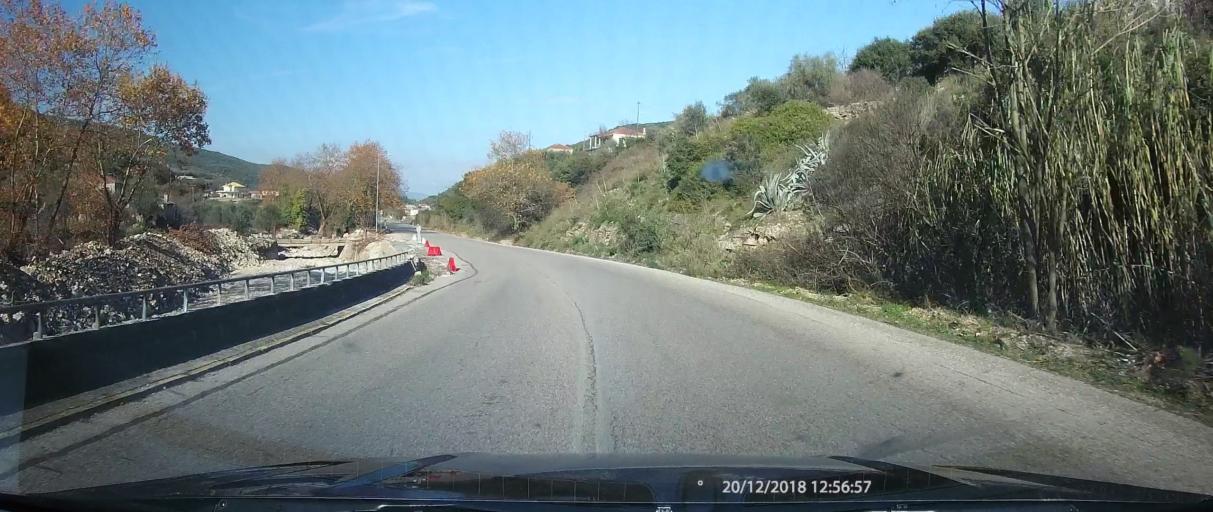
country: GR
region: West Greece
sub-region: Nomos Aitolias kai Akarnanias
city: Pappadhatai
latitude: 38.5168
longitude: 21.3804
